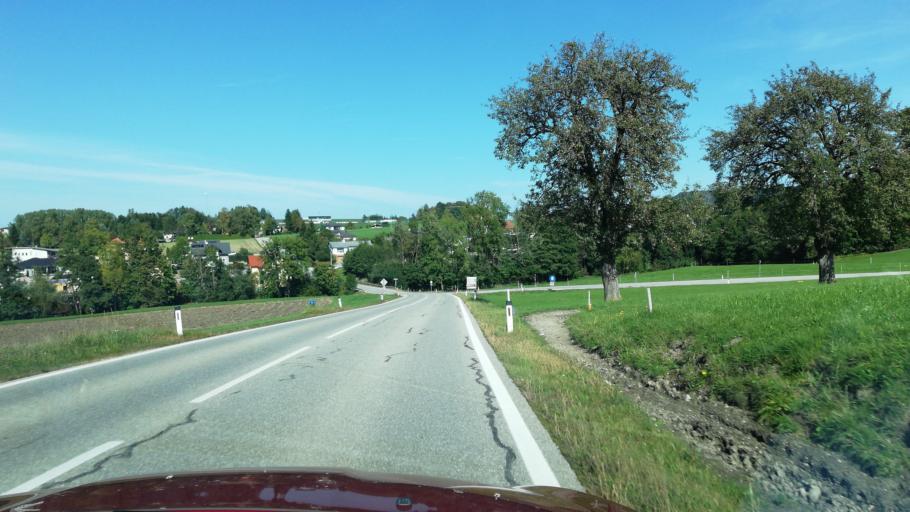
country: AT
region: Upper Austria
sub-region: Politischer Bezirk Vocklabruck
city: Zell am Pettenfirst
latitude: 48.1426
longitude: 13.5703
